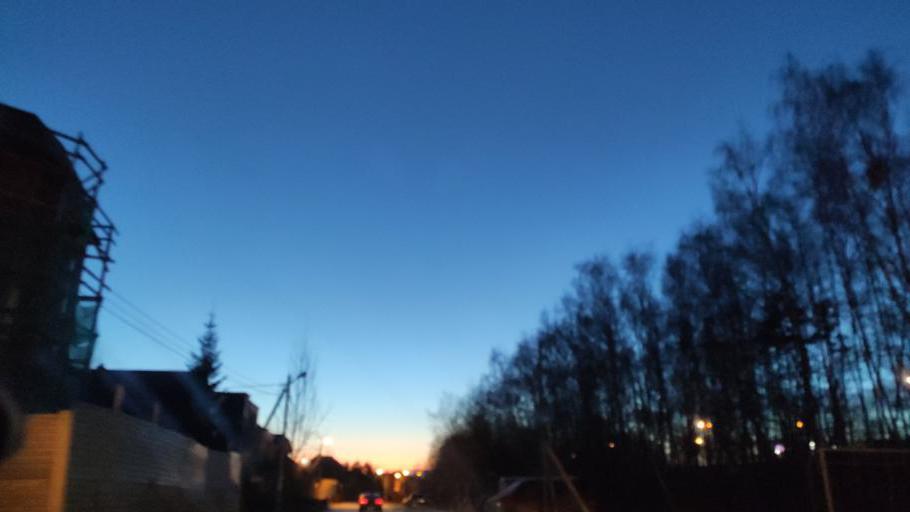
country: RU
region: Moskovskaya
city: Mosrentgen
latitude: 55.6338
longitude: 37.4508
